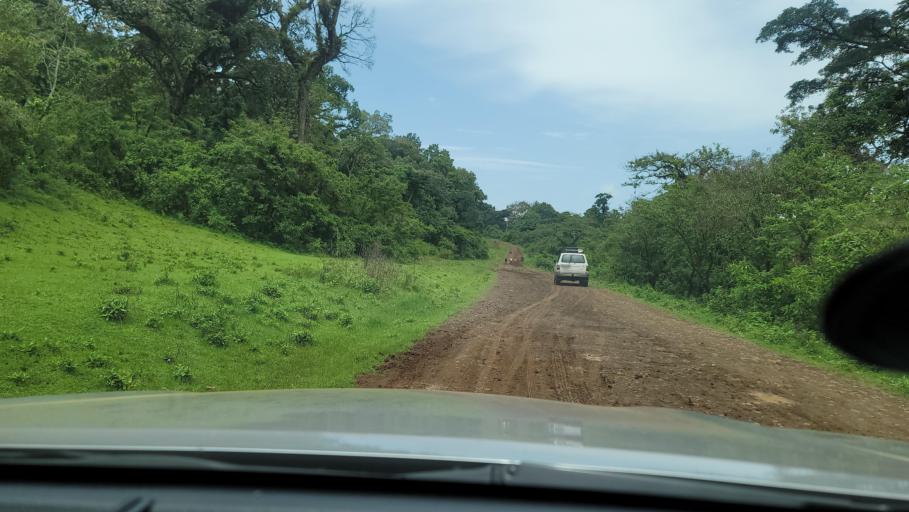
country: ET
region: Oromiya
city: Agaro
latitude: 7.7174
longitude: 36.2587
